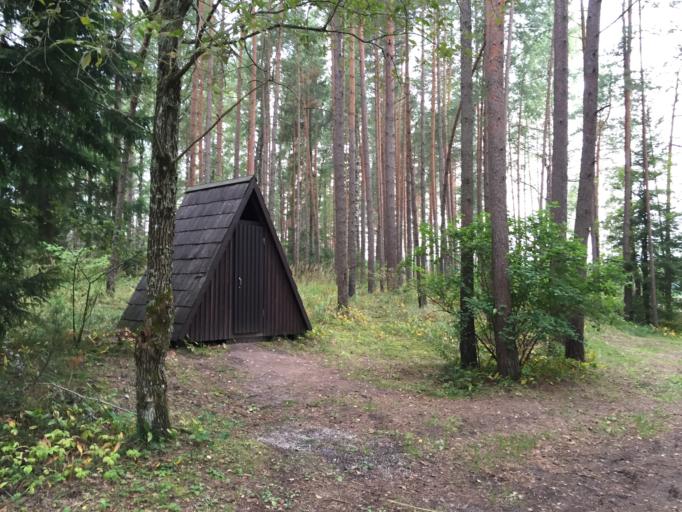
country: LV
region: Ogre
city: Ogre
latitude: 56.8370
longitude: 24.5595
